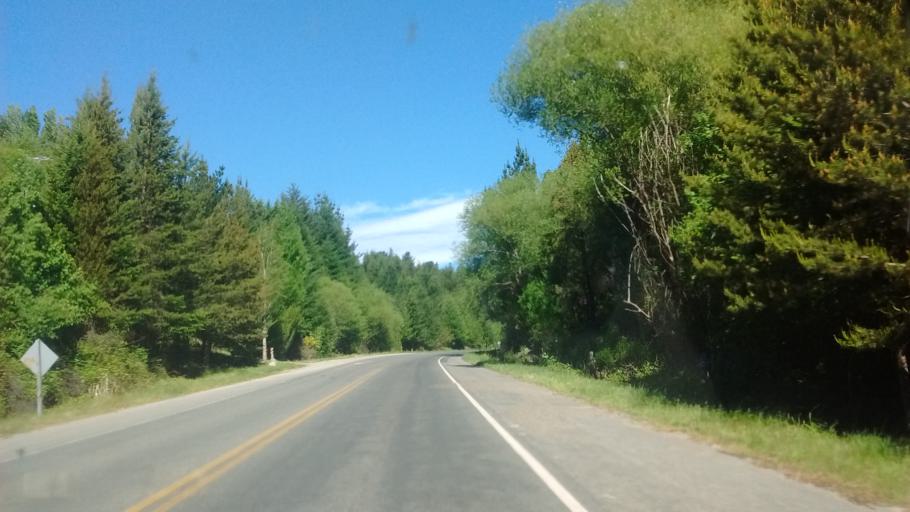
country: AR
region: Chubut
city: Lago Puelo
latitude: -42.0297
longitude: -71.5703
